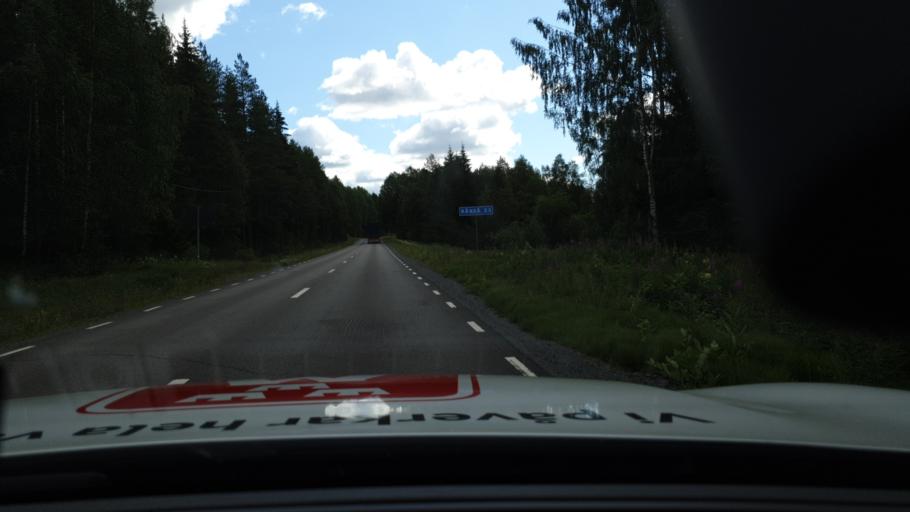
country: SE
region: Norrbotten
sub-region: Lulea Kommun
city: Sodra Sunderbyn
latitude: 65.8318
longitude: 21.9581
